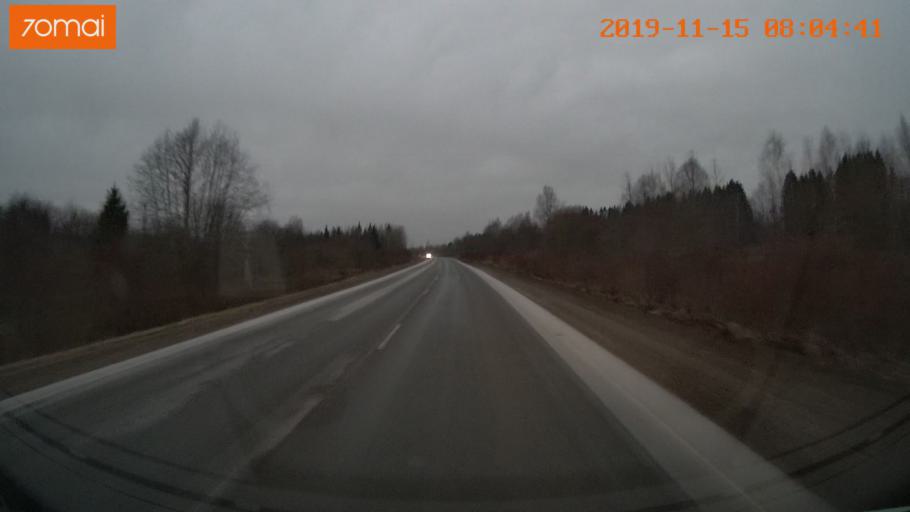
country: RU
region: Vologda
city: Cherepovets
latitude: 59.0107
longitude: 38.0717
